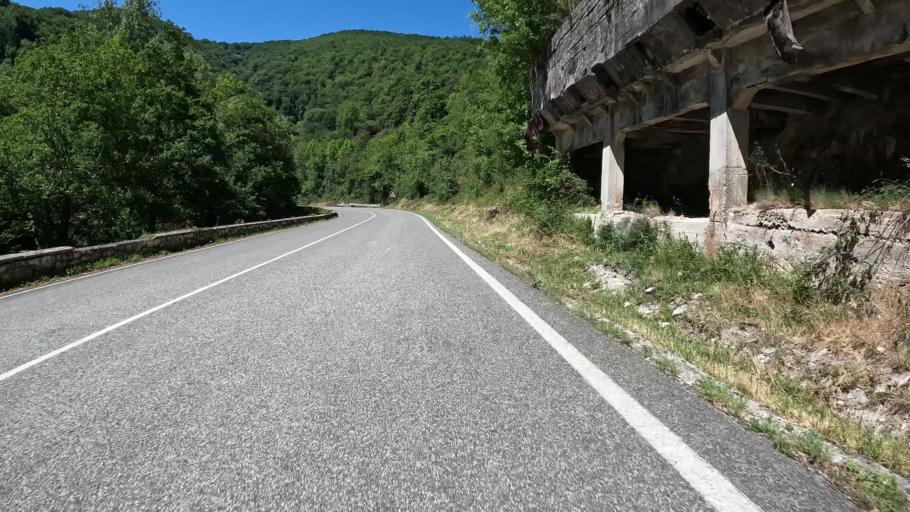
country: ES
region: Basque Country
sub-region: Provincia de Guipuzcoa
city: Oreja
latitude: 43.0709
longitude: -2.0084
